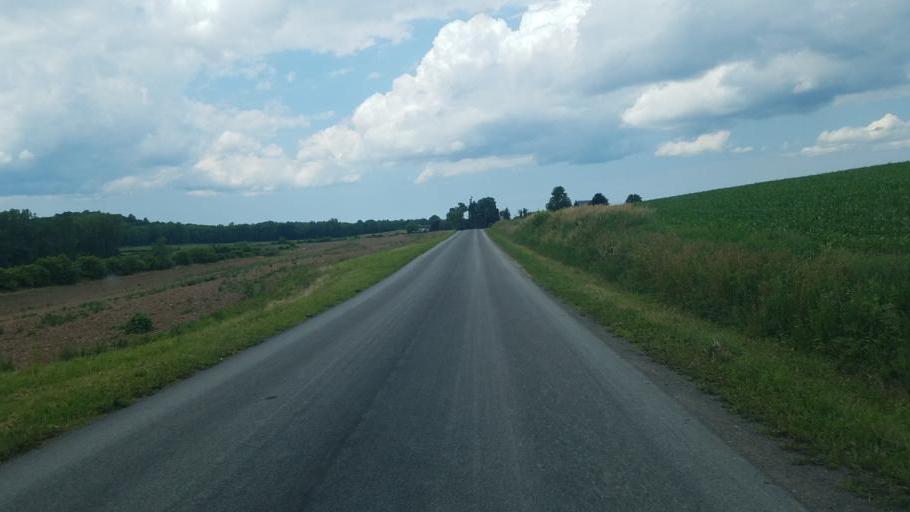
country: US
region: New York
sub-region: Wayne County
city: Clyde
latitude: 43.0296
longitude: -76.8827
